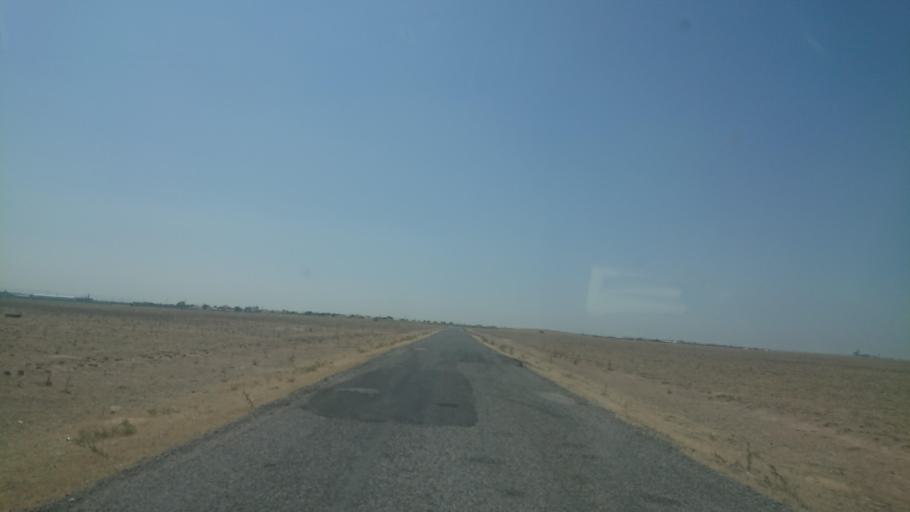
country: TR
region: Aksaray
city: Yesilova
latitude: 38.3033
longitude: 33.7327
